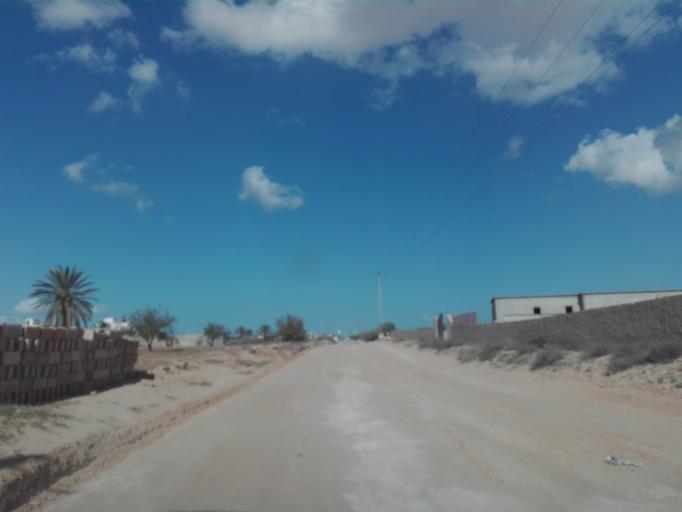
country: TN
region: Madanin
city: Bin Qirdan
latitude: 33.1502
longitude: 11.1925
